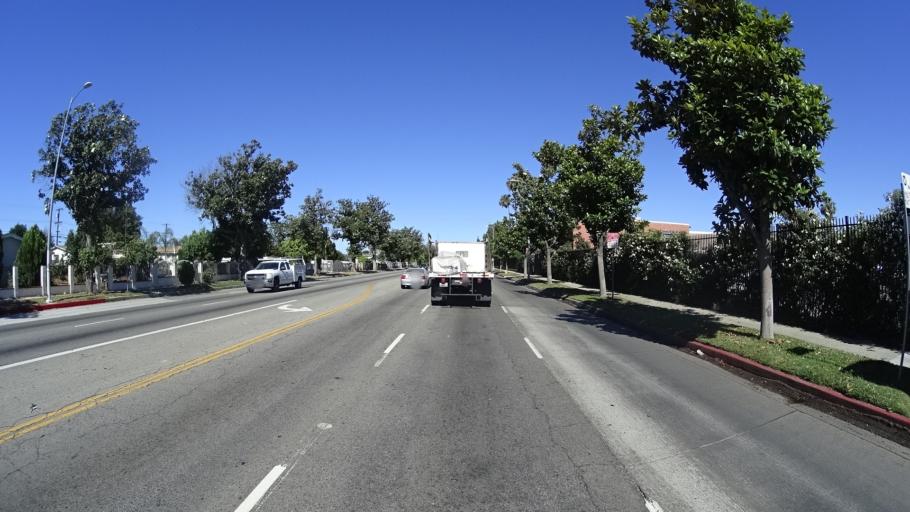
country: US
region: California
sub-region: Los Angeles County
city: Van Nuys
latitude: 34.2217
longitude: -118.4369
